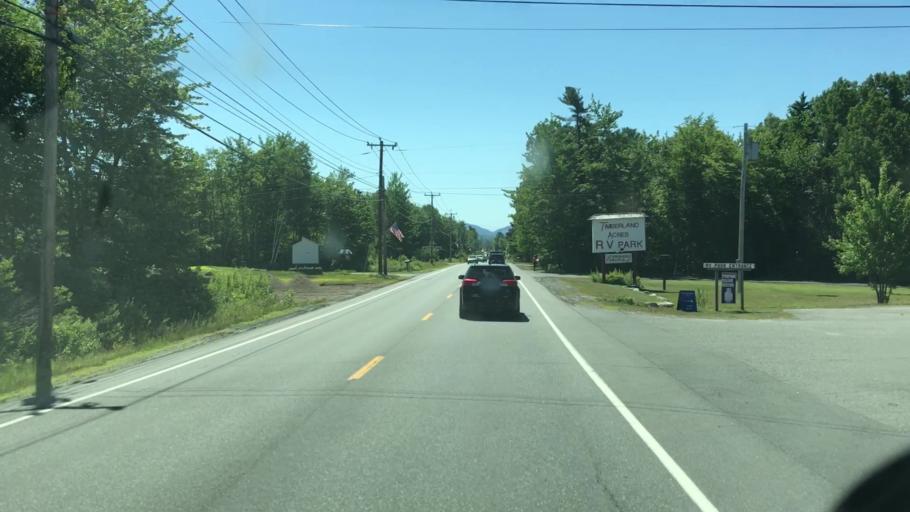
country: US
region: Maine
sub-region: Hancock County
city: Ellsworth
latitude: 44.5074
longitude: -68.3888
